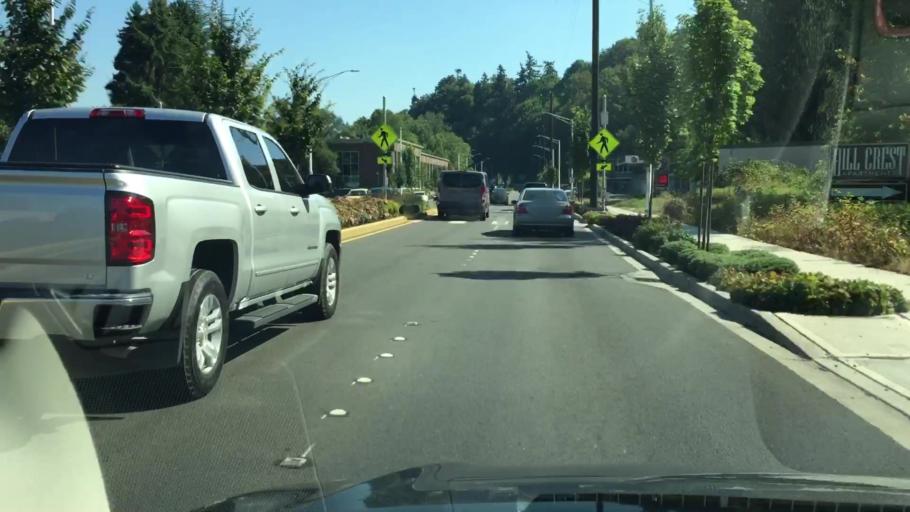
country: US
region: Washington
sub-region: King County
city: Tukwila
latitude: 47.4704
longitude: -122.2540
